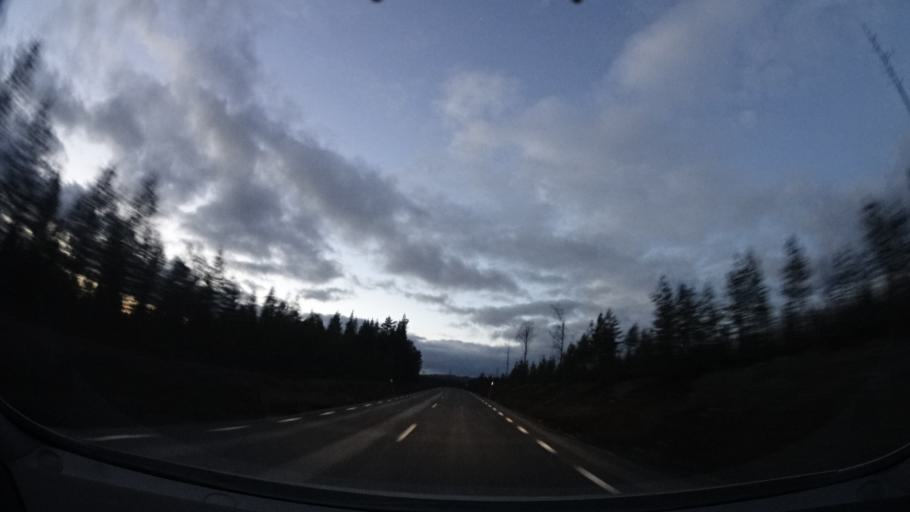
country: SE
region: Vaesterbotten
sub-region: Asele Kommun
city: Asele
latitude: 64.2155
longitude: 16.9068
